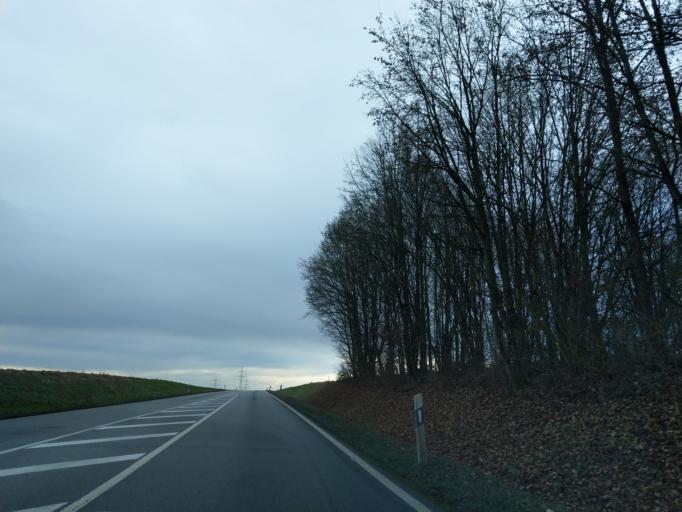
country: DE
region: Bavaria
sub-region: Lower Bavaria
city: Osterhofen
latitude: 48.6629
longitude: 13.0413
